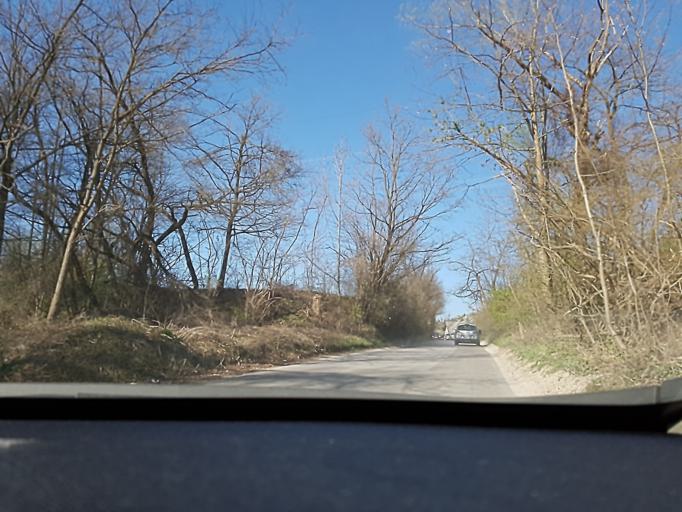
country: SI
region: Trzin
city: Trzin
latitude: 46.0955
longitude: 14.5574
